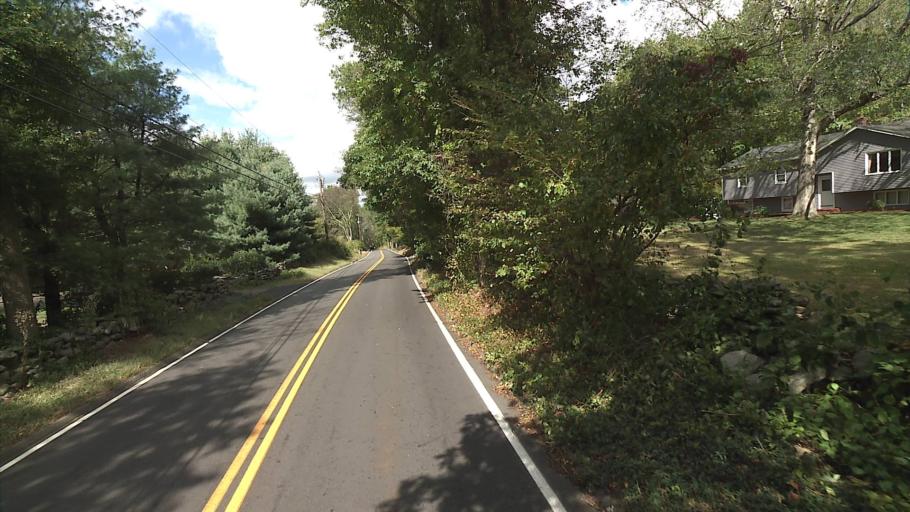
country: US
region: Connecticut
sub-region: Middlesex County
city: Higganum
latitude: 41.3943
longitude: -72.6026
